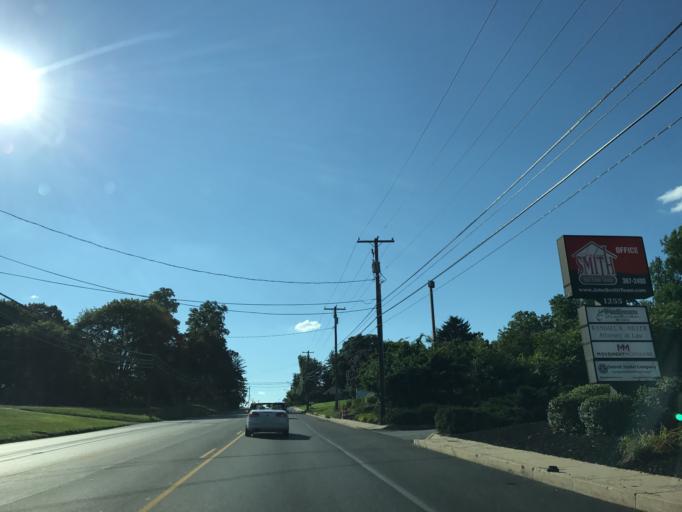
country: US
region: Pennsylvania
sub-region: Lancaster County
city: Elizabethtown
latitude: 40.1405
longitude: -76.5908
